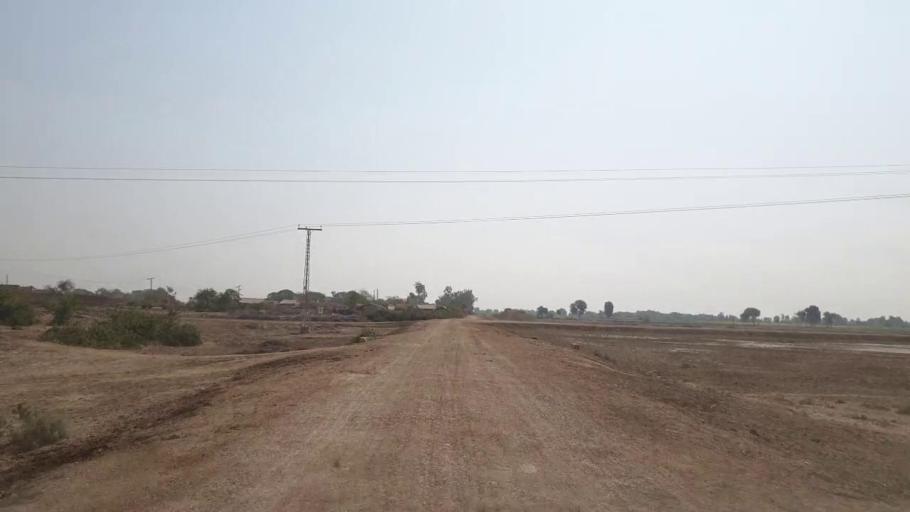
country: PK
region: Sindh
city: Mirpur Khas
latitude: 25.6397
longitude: 69.1466
